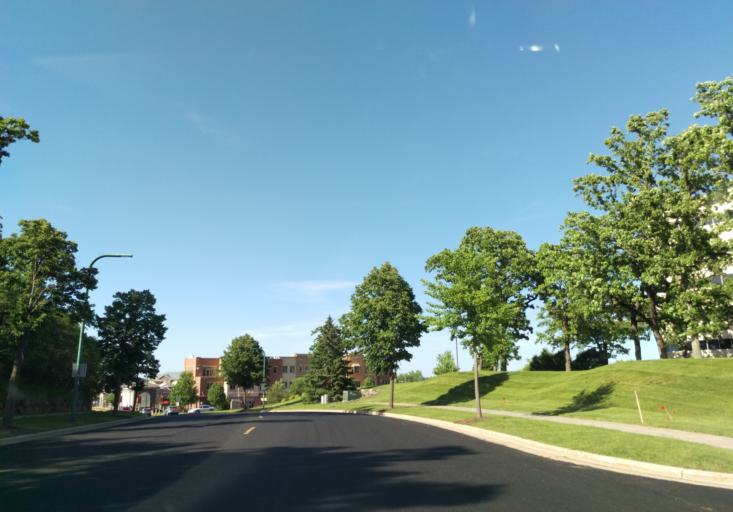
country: US
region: Wisconsin
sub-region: Dane County
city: Middleton
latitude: 43.0884
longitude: -89.5274
